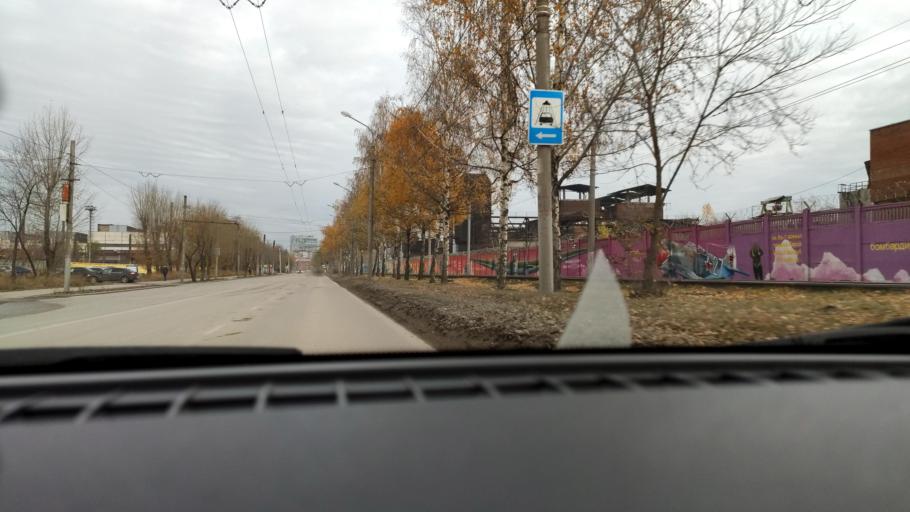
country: RU
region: Perm
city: Perm
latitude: 57.9780
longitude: 56.2467
